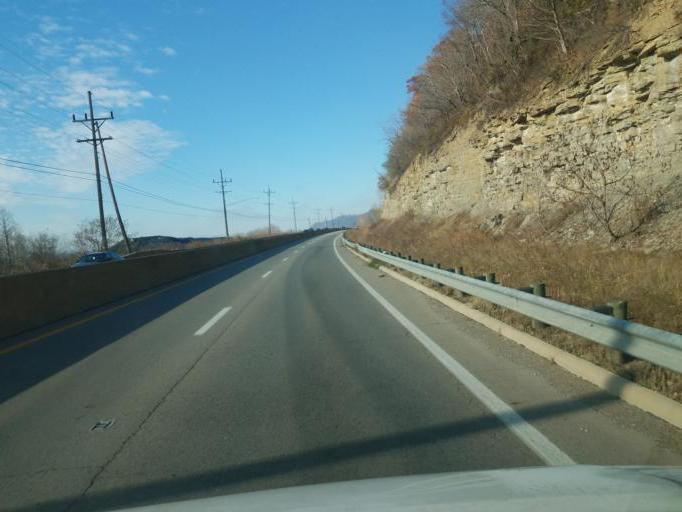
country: US
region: Ohio
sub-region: Scioto County
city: Sciotodale
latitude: 38.7564
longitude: -82.9028
